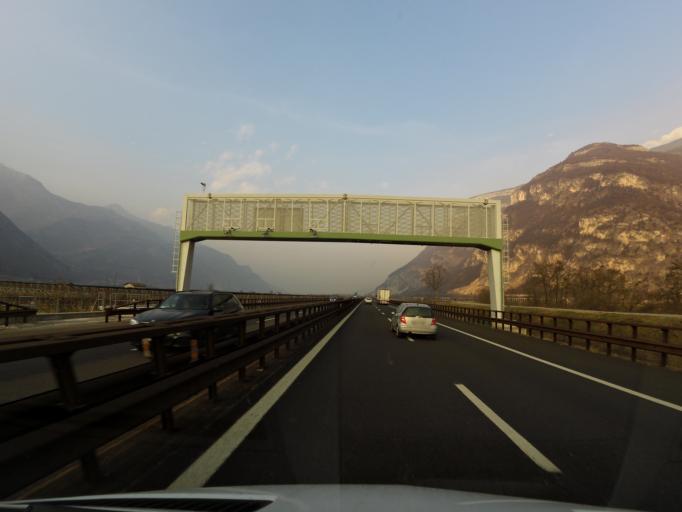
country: IT
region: Trentino-Alto Adige
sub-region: Provincia di Trento
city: Besenello
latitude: 45.9514
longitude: 11.1029
